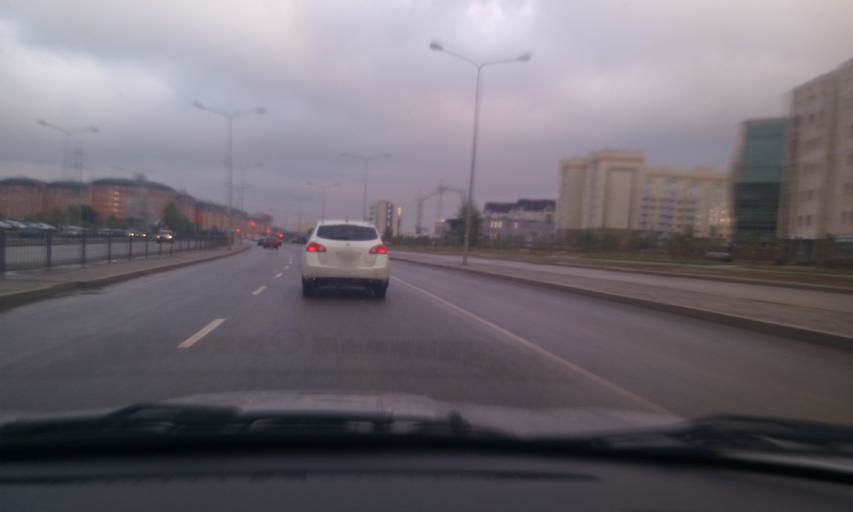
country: KZ
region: Astana Qalasy
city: Astana
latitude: 51.1470
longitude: 71.3777
